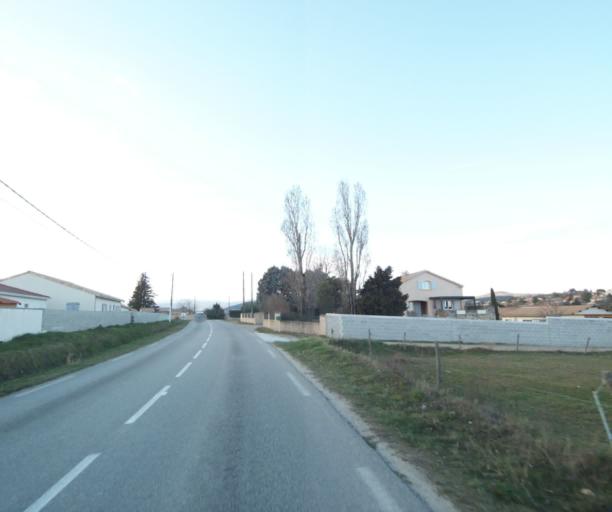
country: FR
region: Rhone-Alpes
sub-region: Departement de l'Ardeche
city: Davezieux
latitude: 45.2458
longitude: 4.7086
